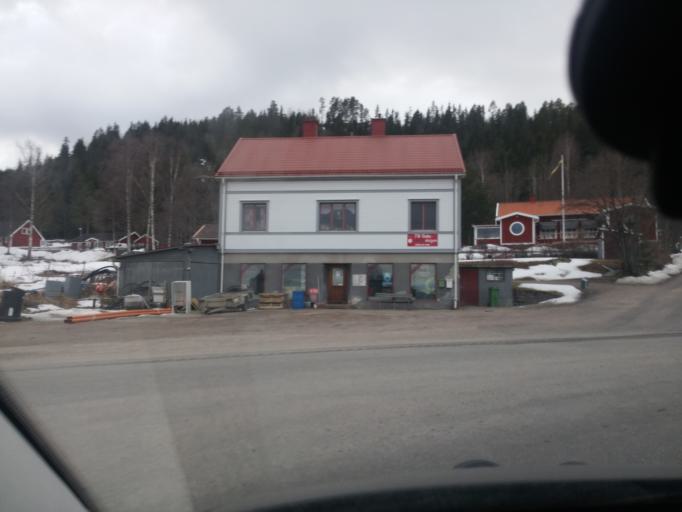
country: SE
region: Gaevleborg
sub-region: Ljusdals Kommun
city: Jaervsoe
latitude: 61.7219
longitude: 16.1678
